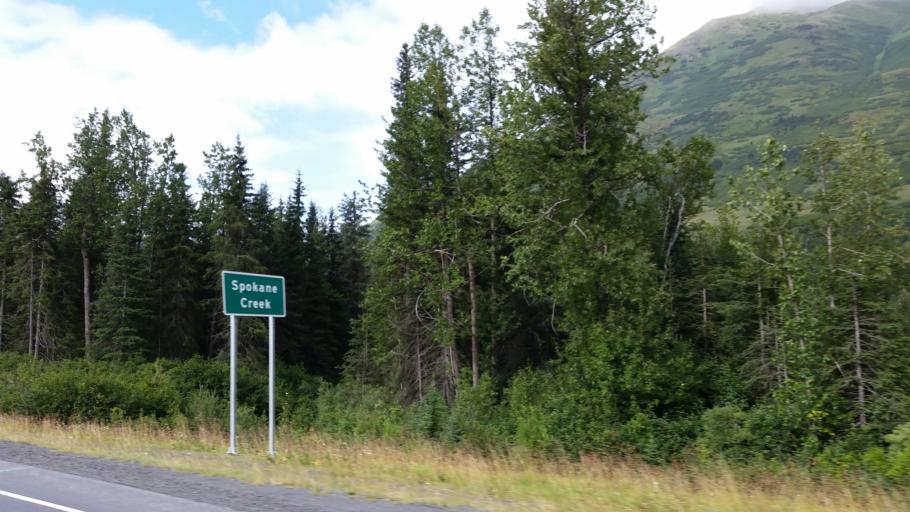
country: US
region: Alaska
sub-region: Anchorage Municipality
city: Girdwood
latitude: 60.7418
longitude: -149.2594
